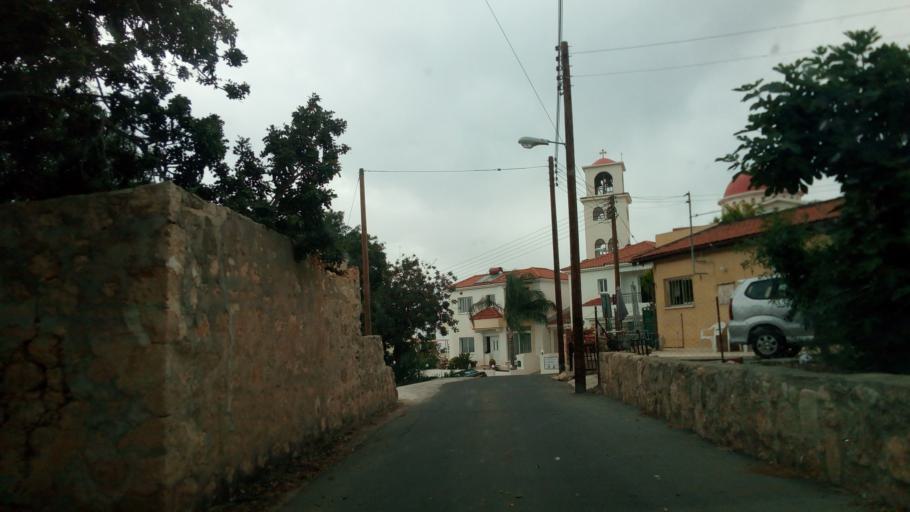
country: CY
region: Pafos
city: Mesogi
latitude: 34.8155
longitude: 32.4441
